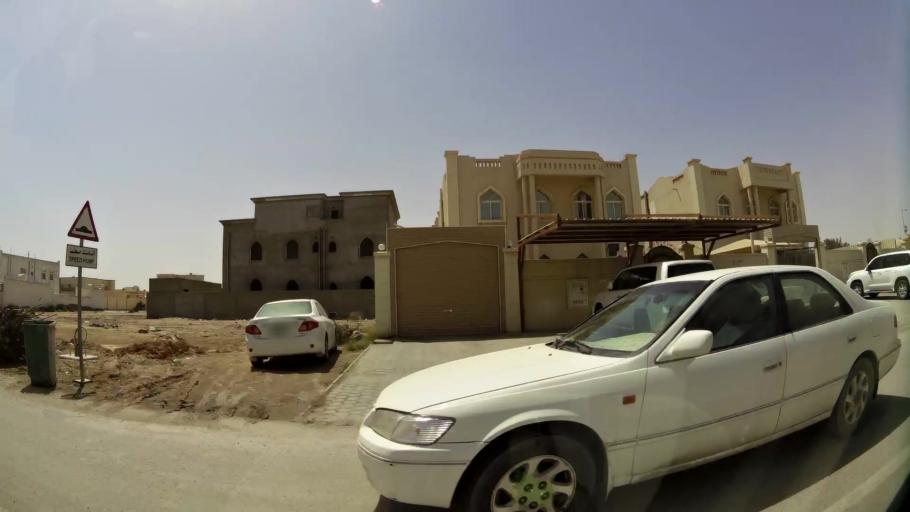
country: QA
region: Baladiyat Umm Salal
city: Umm Salal Muhammad
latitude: 25.3773
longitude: 51.4467
